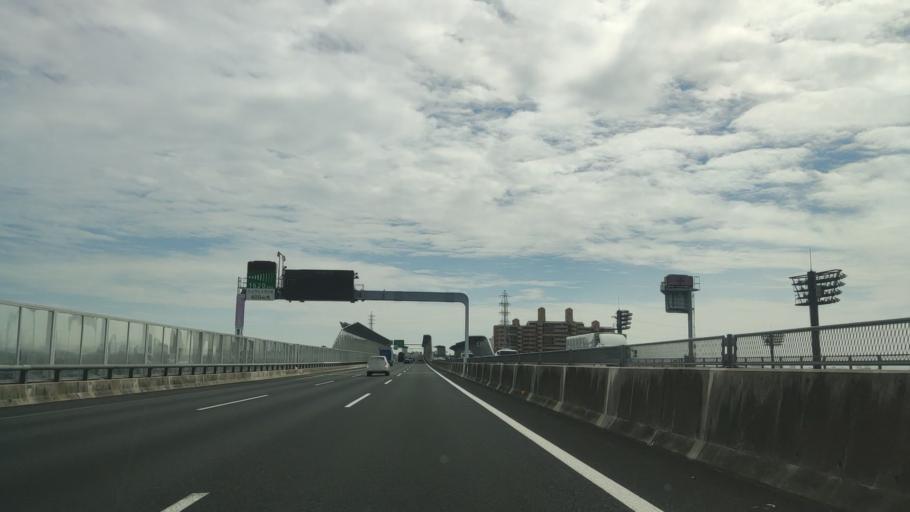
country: JP
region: Aichi
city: Chiryu
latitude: 35.0307
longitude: 137.0600
